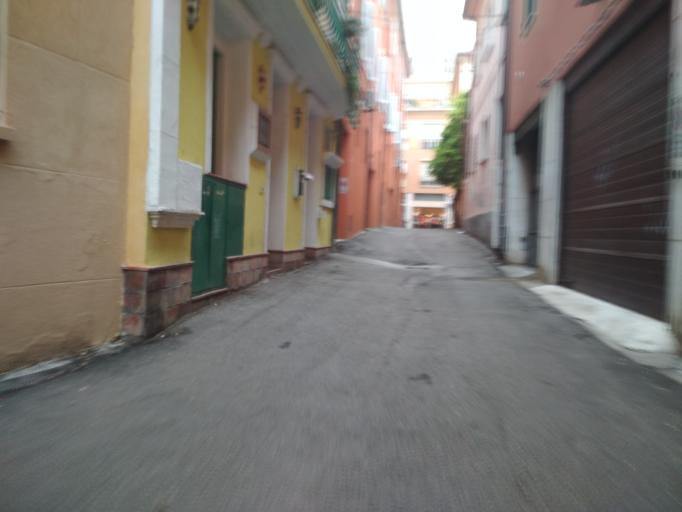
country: IT
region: Emilia-Romagna
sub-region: Provincia di Rimini
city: Rimini
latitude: 44.0589
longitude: 12.5676
